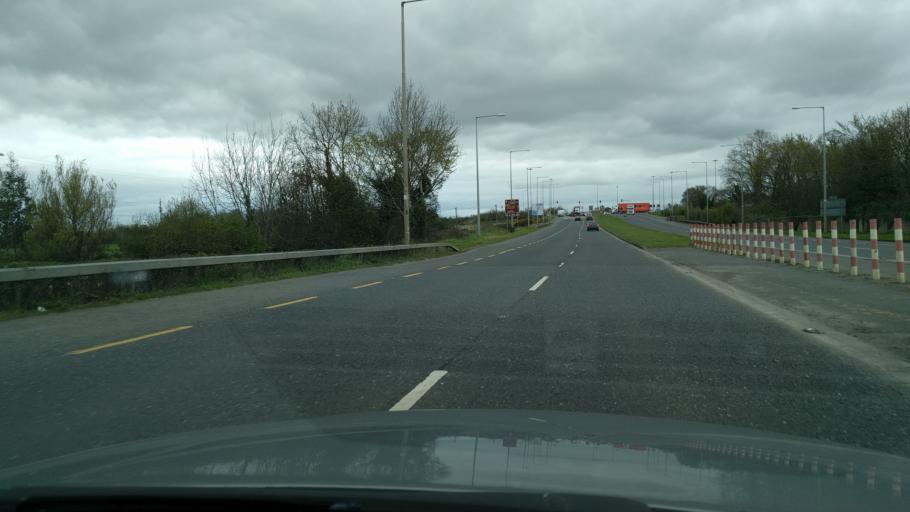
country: IE
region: Leinster
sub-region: Fingal County
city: Swords
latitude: 53.4744
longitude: -6.2088
